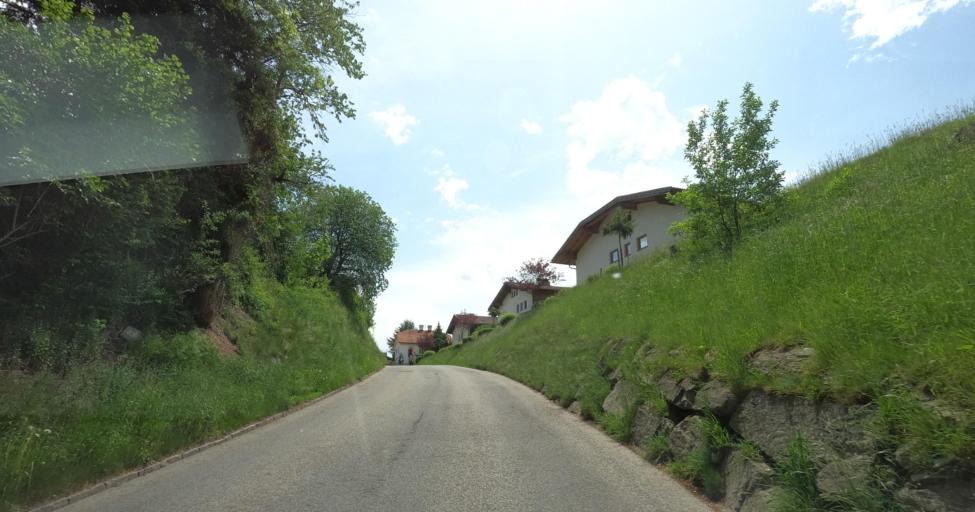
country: AT
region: Tyrol
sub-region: Politischer Bezirk Innsbruck Land
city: Schoenberg im Stubaital
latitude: 47.1873
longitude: 11.4289
